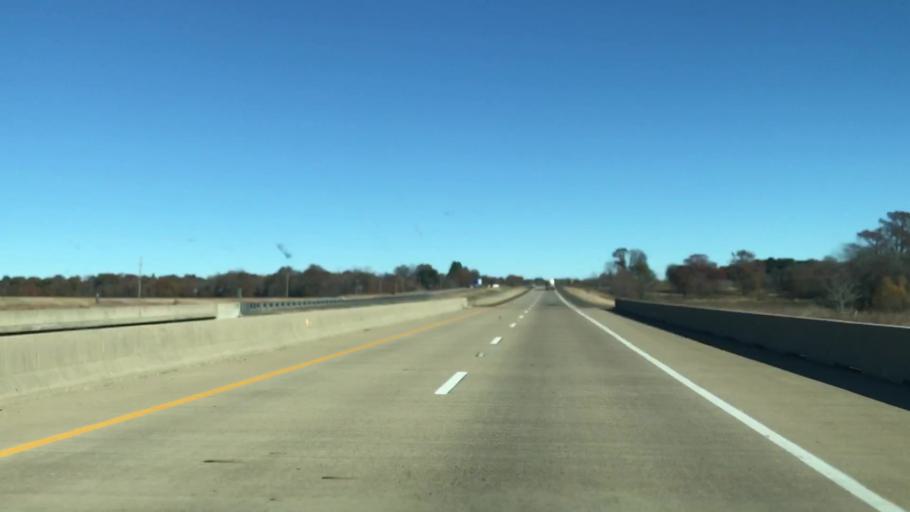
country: US
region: Texas
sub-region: Cass County
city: Queen City
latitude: 33.1494
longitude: -93.8909
